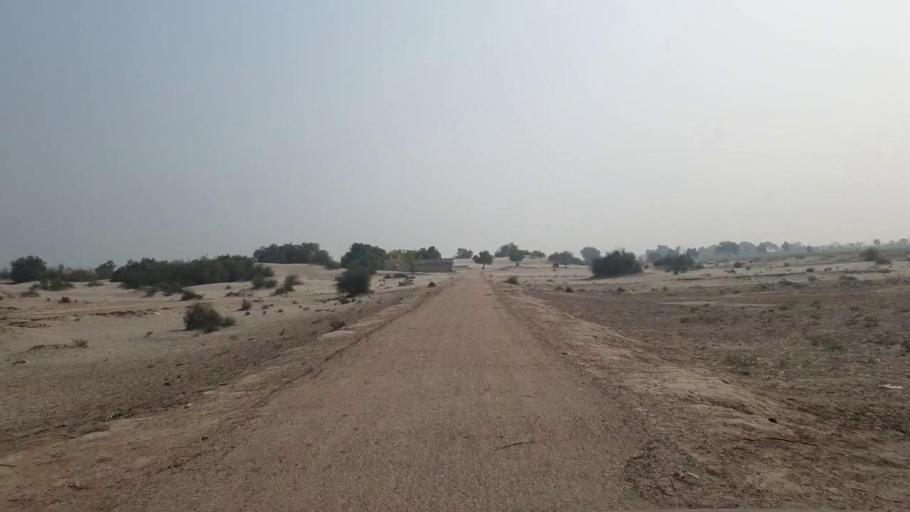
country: PK
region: Sindh
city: Hala
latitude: 25.8251
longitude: 68.4452
